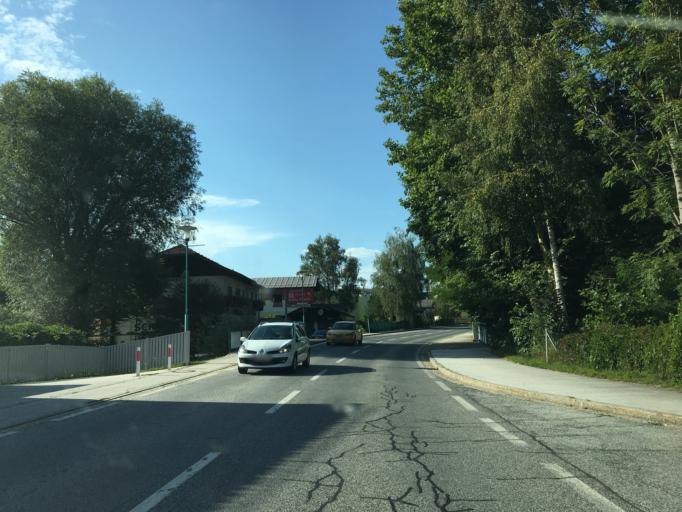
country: AT
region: Carinthia
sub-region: Politischer Bezirk Volkermarkt
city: Eberndorf
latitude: 46.6201
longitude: 14.6345
